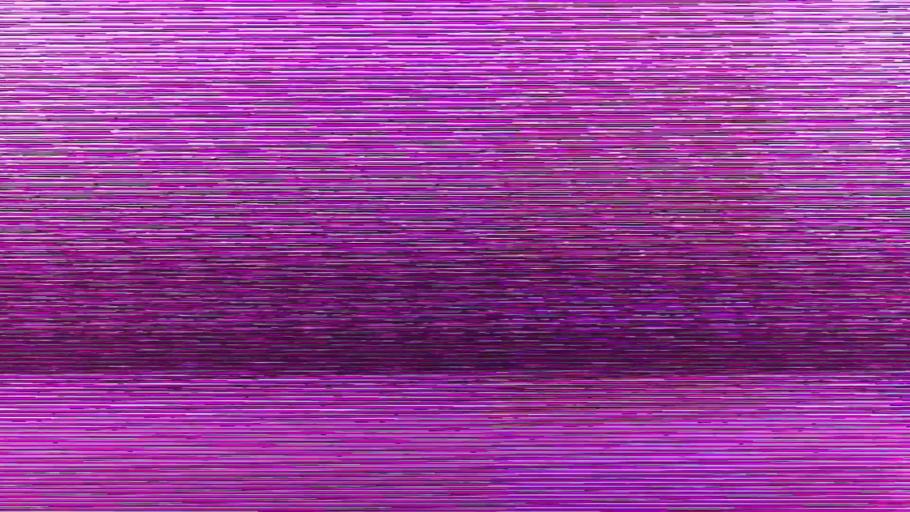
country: US
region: Michigan
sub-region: Oakland County
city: Sylvan Lake
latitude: 42.6276
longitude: -83.3174
